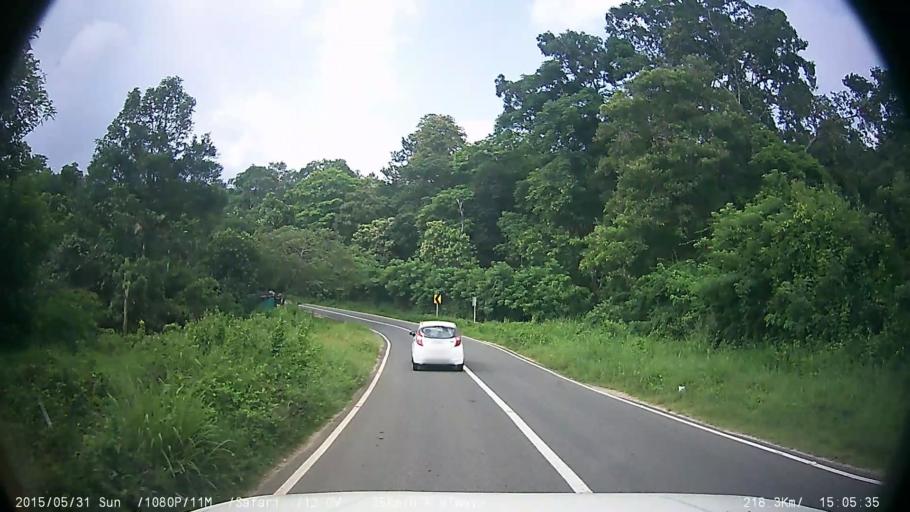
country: IN
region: Kerala
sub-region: Wayanad
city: Kalpetta
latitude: 11.6388
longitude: 76.2146
